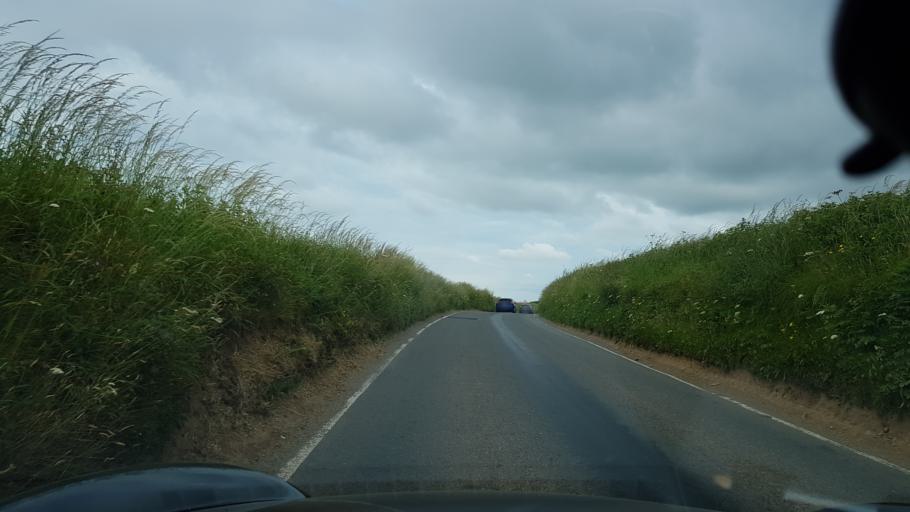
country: GB
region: Wales
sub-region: Pembrokeshire
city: Herbrandston
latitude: 51.7592
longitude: -5.1063
